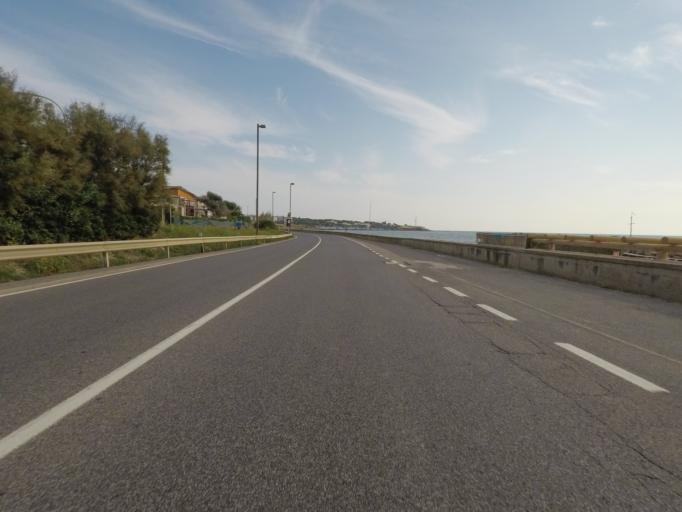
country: IT
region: Latium
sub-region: Citta metropolitana di Roma Capitale
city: Santa Marinella
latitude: 42.0412
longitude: 11.8278
